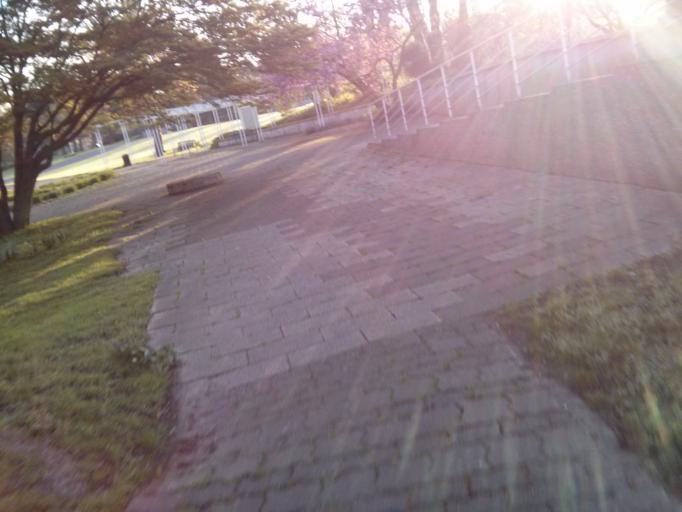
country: DE
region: North Rhine-Westphalia
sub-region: Regierungsbezirk Koln
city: Deutz
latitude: 50.9504
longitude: 6.9769
